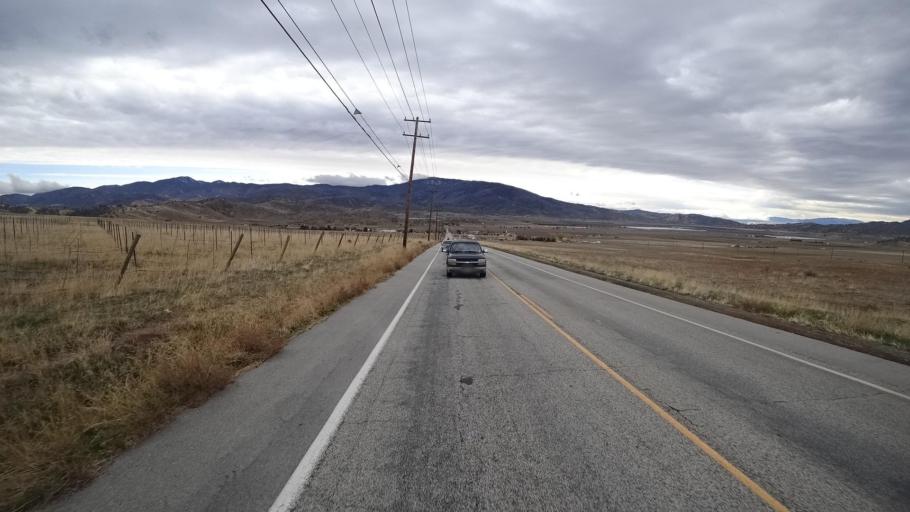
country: US
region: California
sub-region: Kern County
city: Bear Valley Springs
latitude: 35.1433
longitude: -118.5754
